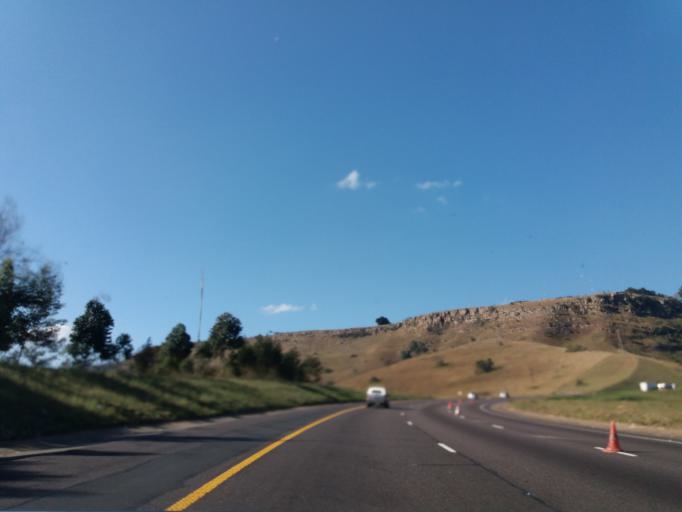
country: ZA
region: KwaZulu-Natal
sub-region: eThekwini Metropolitan Municipality
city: Mpumalanga
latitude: -29.7773
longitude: 30.7046
